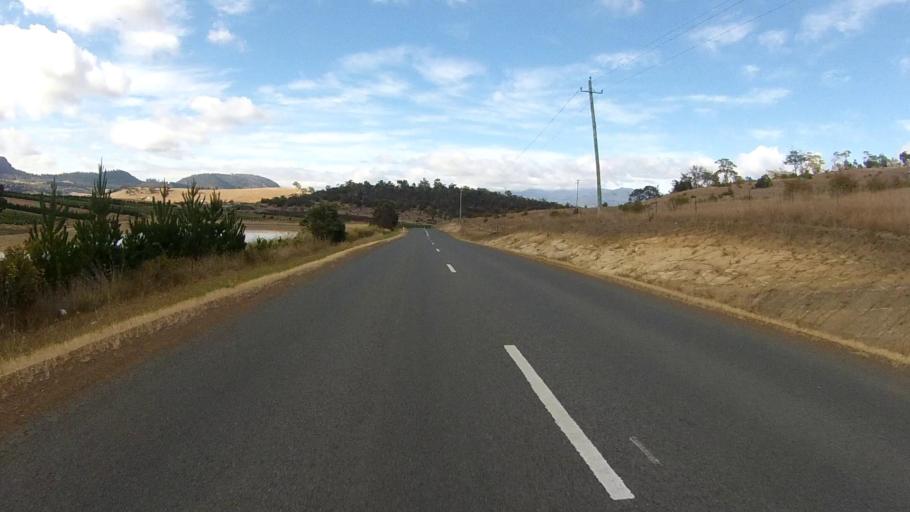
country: AU
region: Tasmania
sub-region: Brighton
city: Old Beach
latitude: -42.7378
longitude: 147.2883
